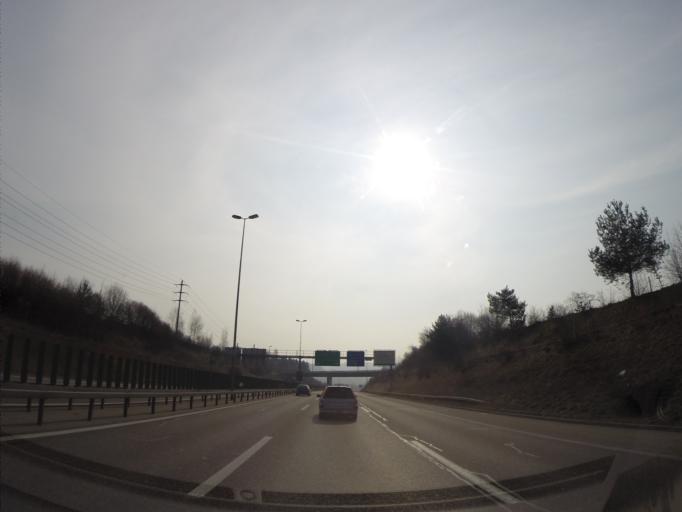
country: CH
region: Zurich
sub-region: Bezirk Winterthur
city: Wuelflingen (Kreis 6) / Lindenplatz
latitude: 47.5197
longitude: 8.6968
